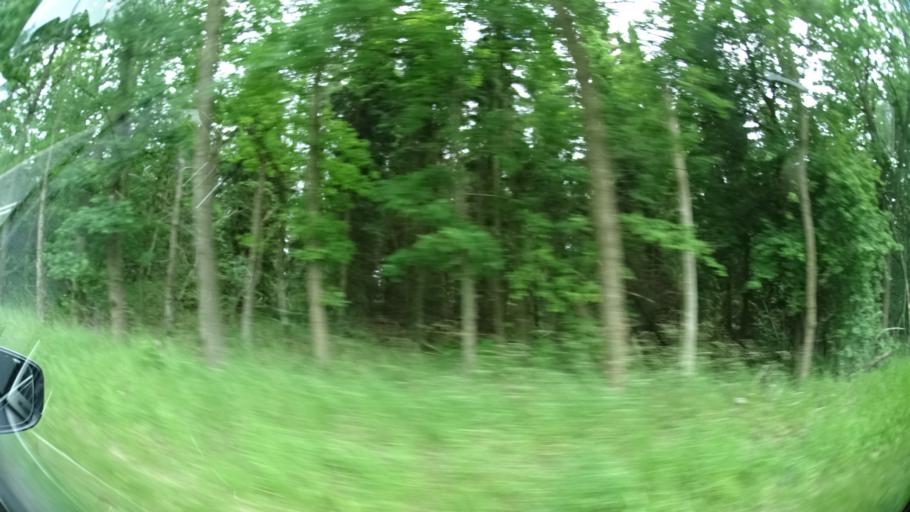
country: DK
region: Central Jutland
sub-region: Syddjurs Kommune
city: Ryomgard
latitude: 56.3635
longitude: 10.4958
